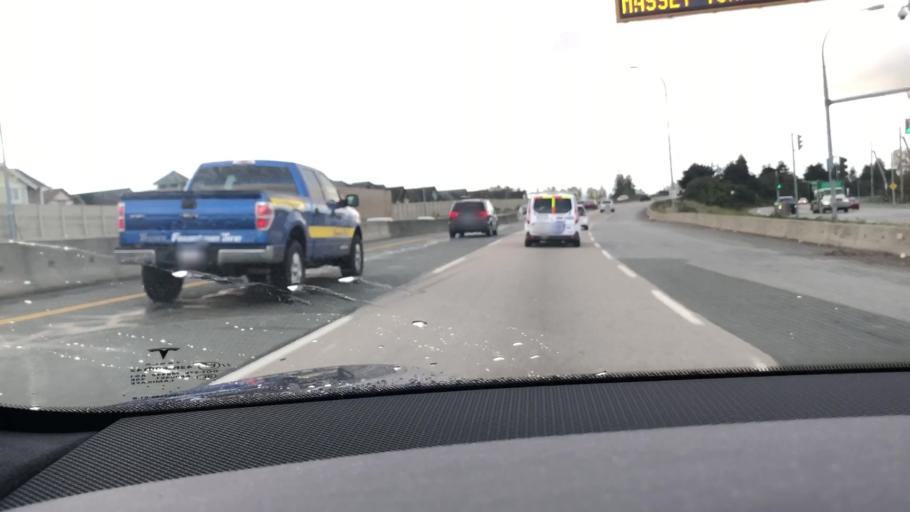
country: CA
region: British Columbia
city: New Westminster
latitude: 49.1834
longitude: -122.9529
